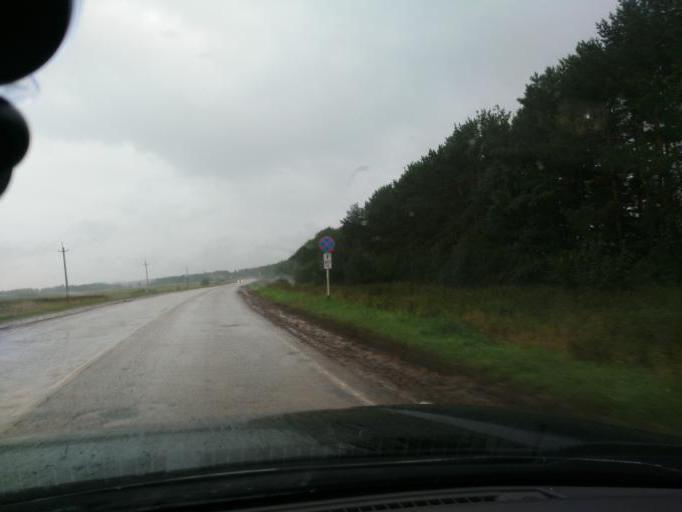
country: RU
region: Perm
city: Osa
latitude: 57.2906
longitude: 55.5836
